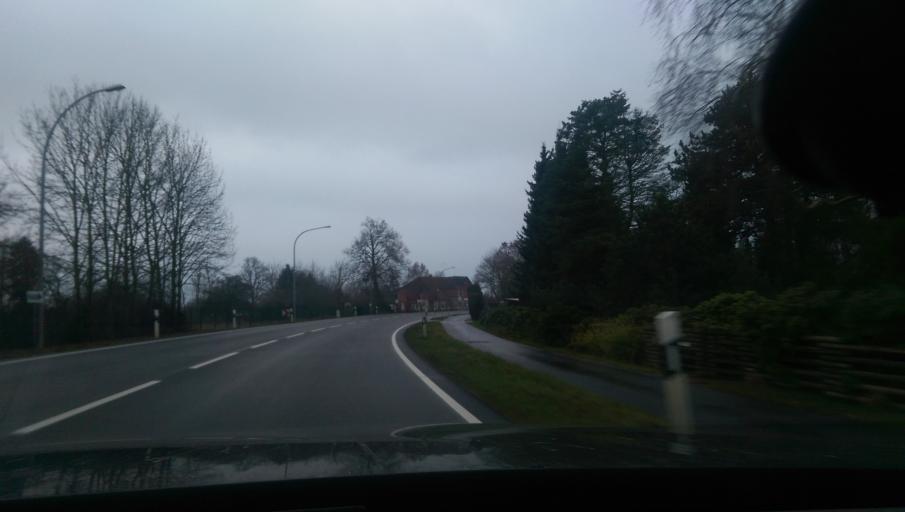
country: DE
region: Lower Saxony
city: Dorverden
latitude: 52.8868
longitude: 9.2213
